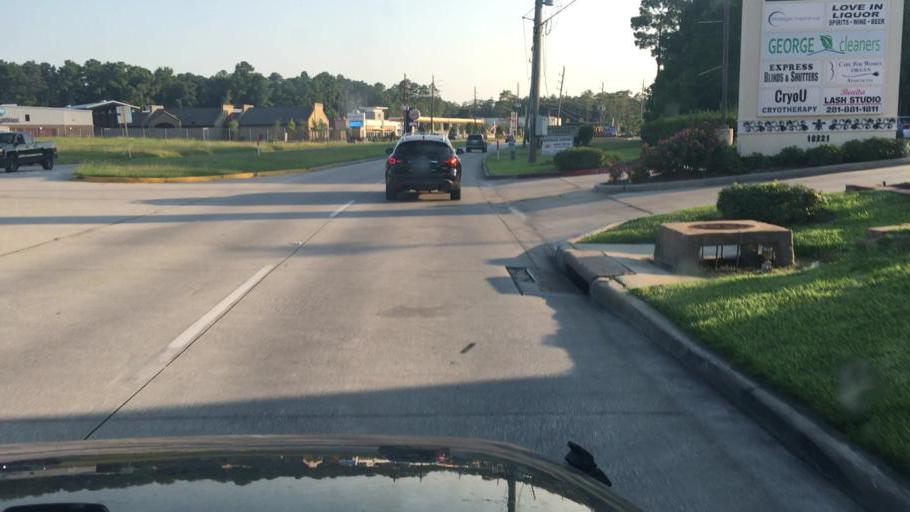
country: US
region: Texas
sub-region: Harris County
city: Atascocita
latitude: 29.9823
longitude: -95.1627
